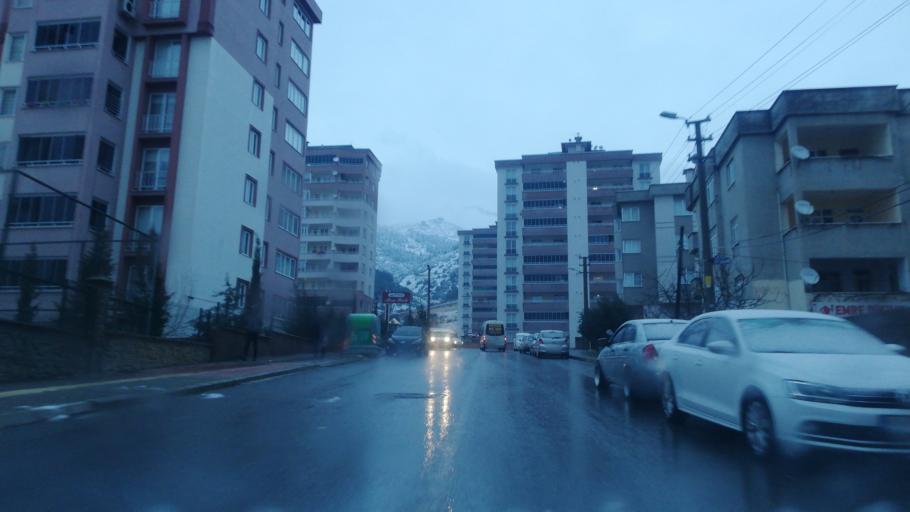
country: TR
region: Kahramanmaras
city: Kahramanmaras
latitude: 37.5998
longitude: 36.8824
